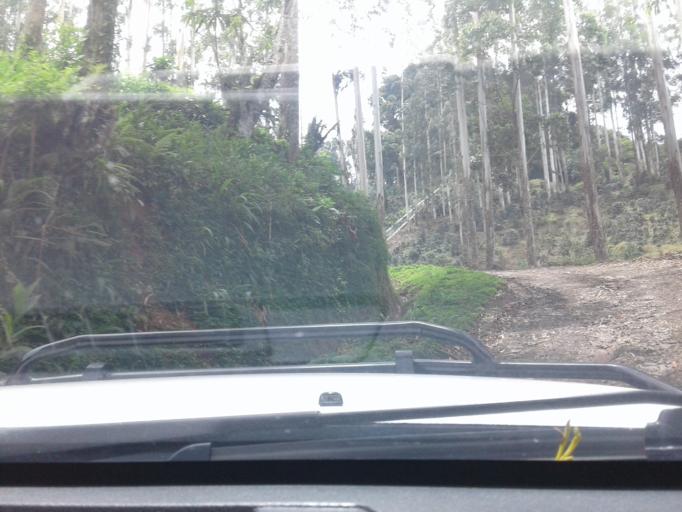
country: NI
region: Matagalpa
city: Matagalpa
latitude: 13.0496
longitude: -85.8768
